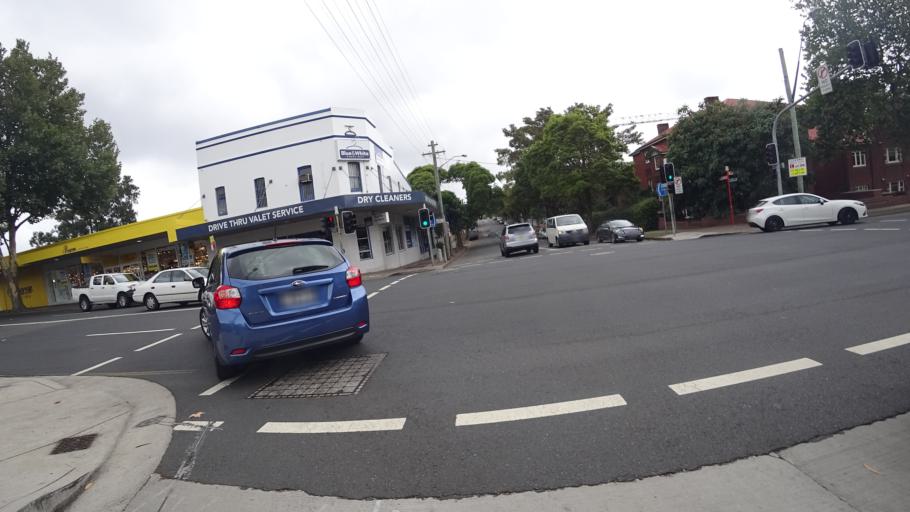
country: AU
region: New South Wales
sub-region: North Sydney
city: Crows Nest
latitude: -33.8286
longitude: 151.2063
